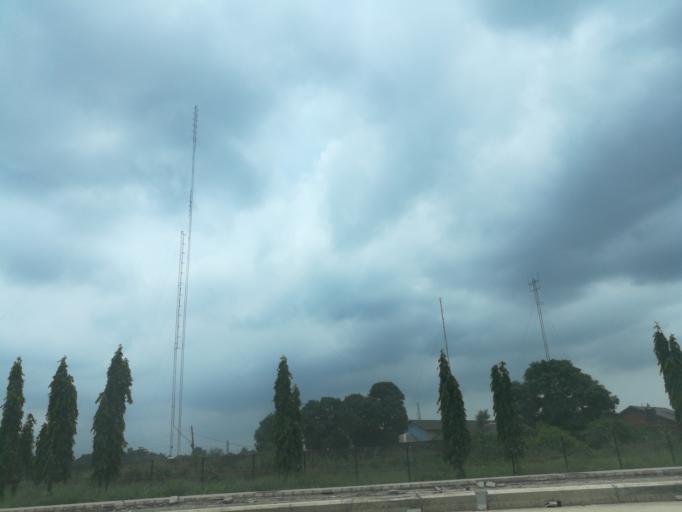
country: NG
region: Lagos
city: Oshodi
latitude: 6.5684
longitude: 3.3466
